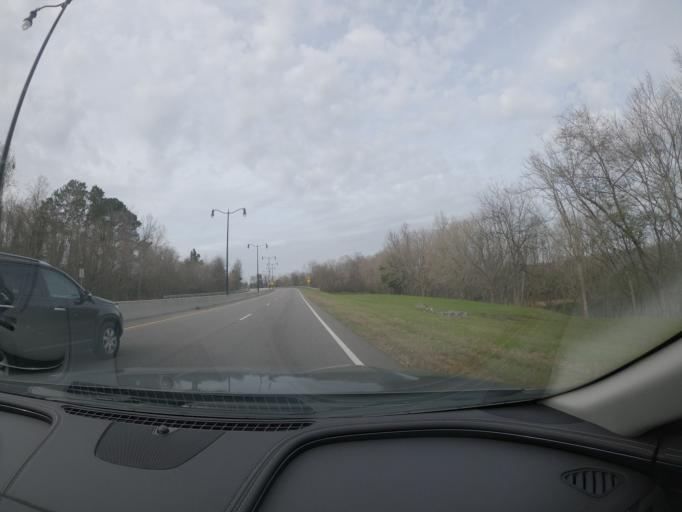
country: US
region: South Carolina
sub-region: Aiken County
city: North Augusta
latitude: 33.5035
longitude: -81.9966
